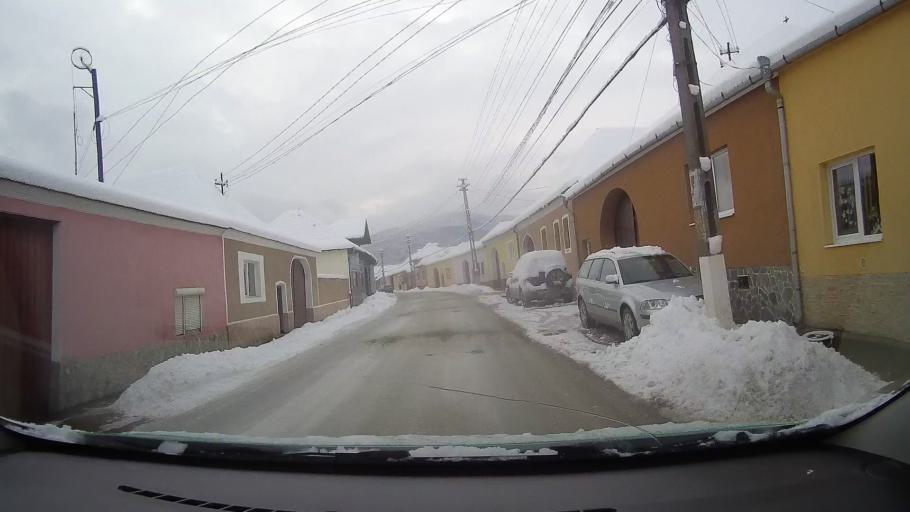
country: RO
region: Alba
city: Pianu de Sus
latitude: 45.9009
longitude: 23.4804
